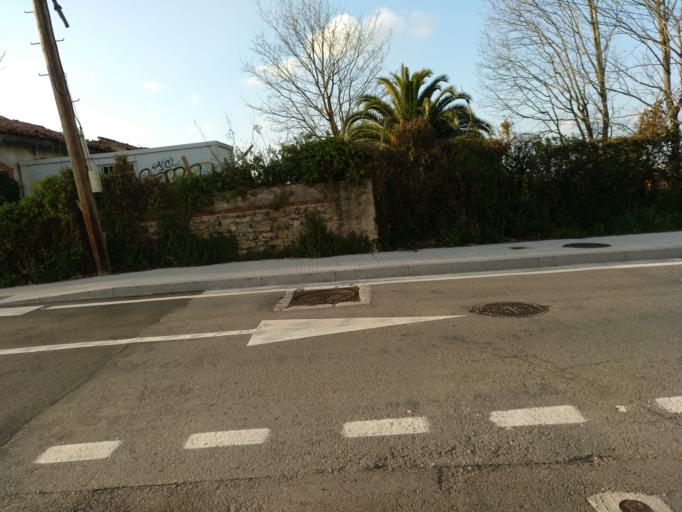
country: ES
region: Asturias
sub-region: Province of Asturias
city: Gijon
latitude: 43.5152
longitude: -5.6643
